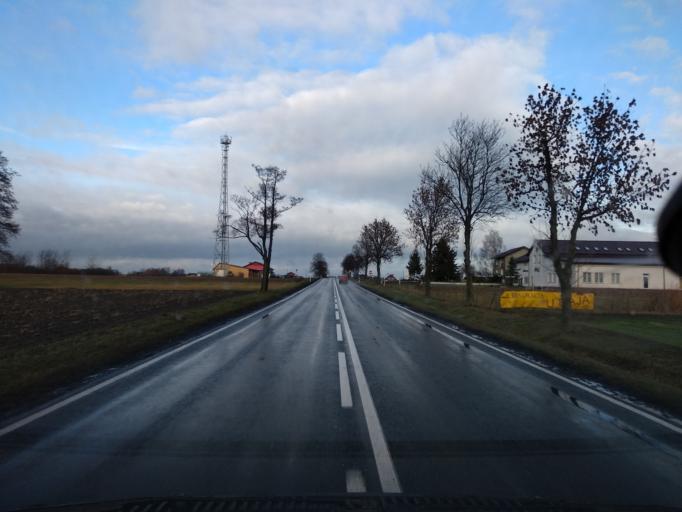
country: PL
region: Greater Poland Voivodeship
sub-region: Powiat koninski
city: Rychwal
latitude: 52.0527
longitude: 18.1630
